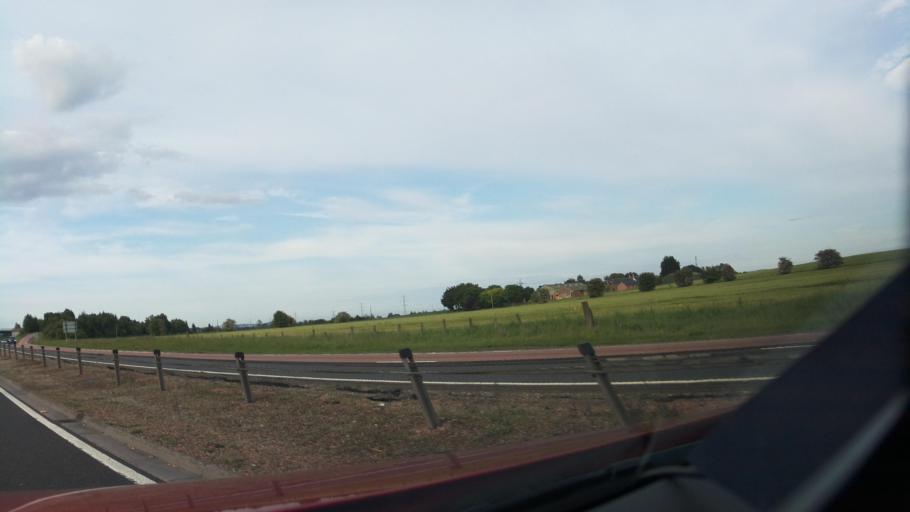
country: GB
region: Scotland
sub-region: Perth and Kinross
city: Errol
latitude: 56.4168
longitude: -3.2377
